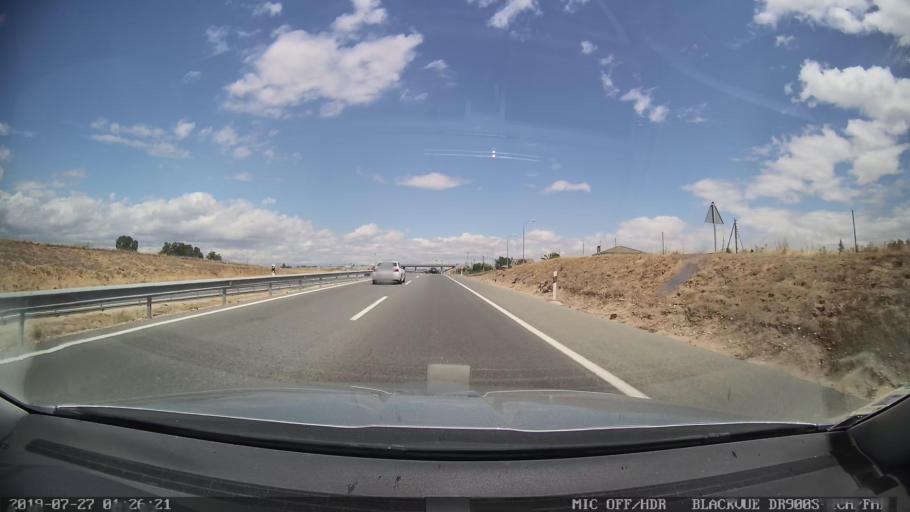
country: ES
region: Castille-La Mancha
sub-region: Province of Toledo
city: La Torre de Esteban Hambran
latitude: 40.1553
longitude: -4.1740
